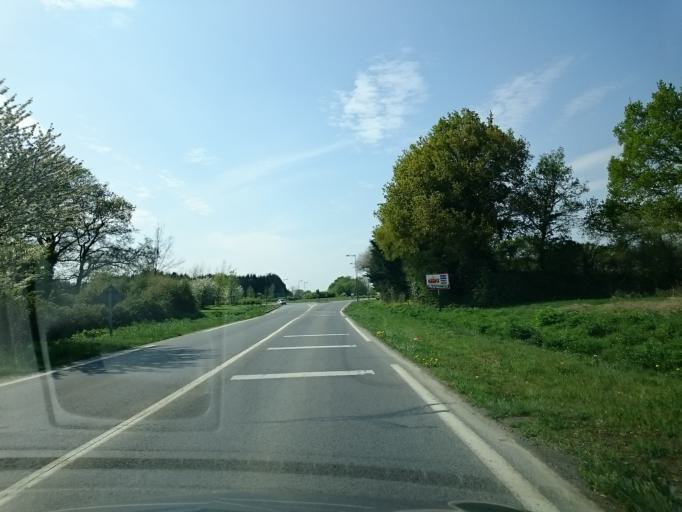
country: FR
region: Brittany
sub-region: Departement d'Ille-et-Vilaine
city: Chantepie
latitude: 48.0796
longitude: -1.6022
